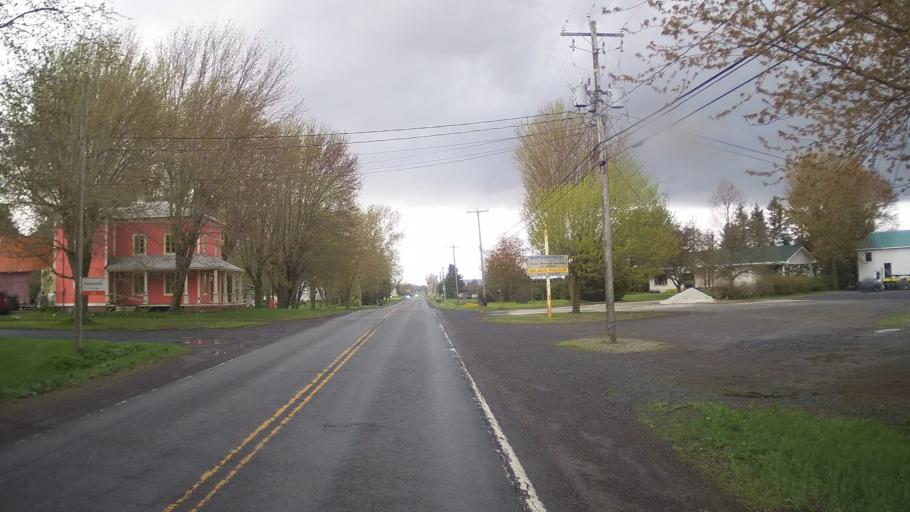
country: CA
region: Quebec
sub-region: Monteregie
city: Rougemont
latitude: 45.3397
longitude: -73.0888
